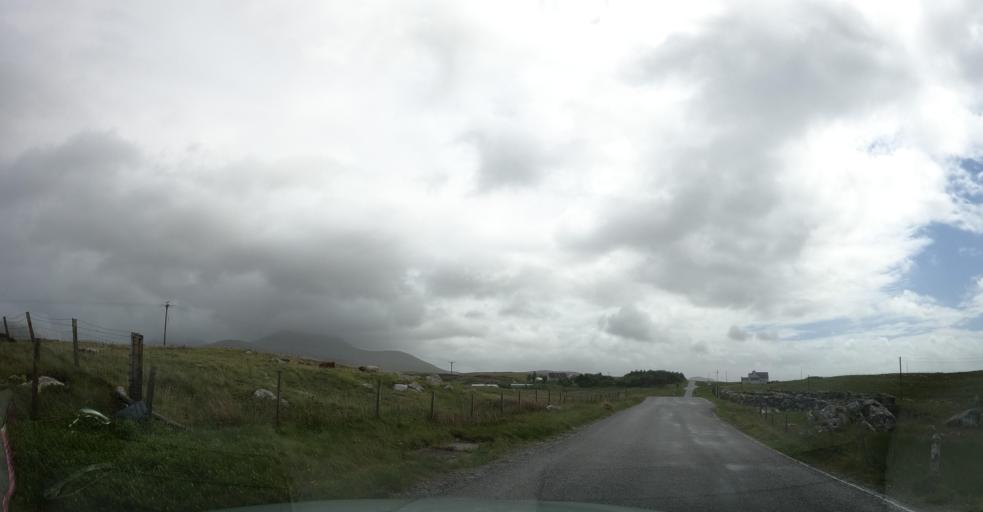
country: GB
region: Scotland
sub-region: Eilean Siar
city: Isle of South Uist
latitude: 57.2896
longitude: -7.3669
